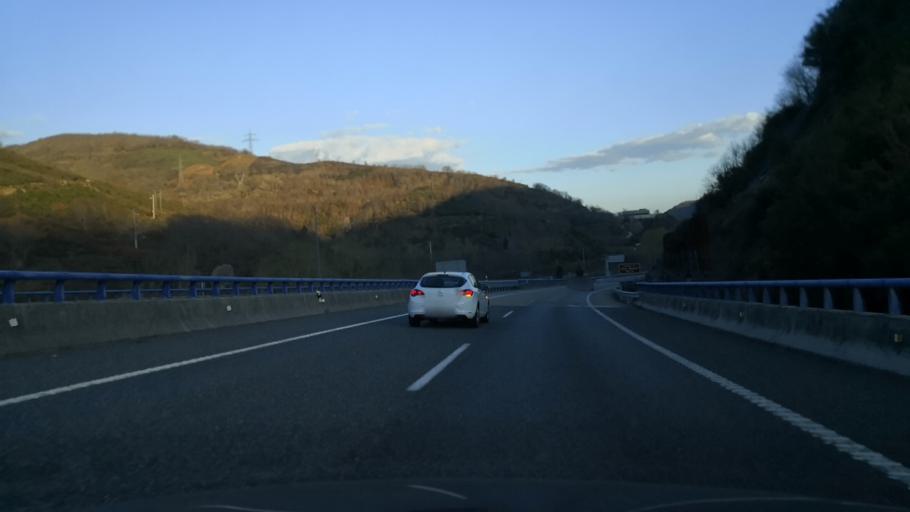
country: ES
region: Castille and Leon
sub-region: Provincia de Leon
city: Trabadelo
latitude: 42.6554
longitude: -6.8948
